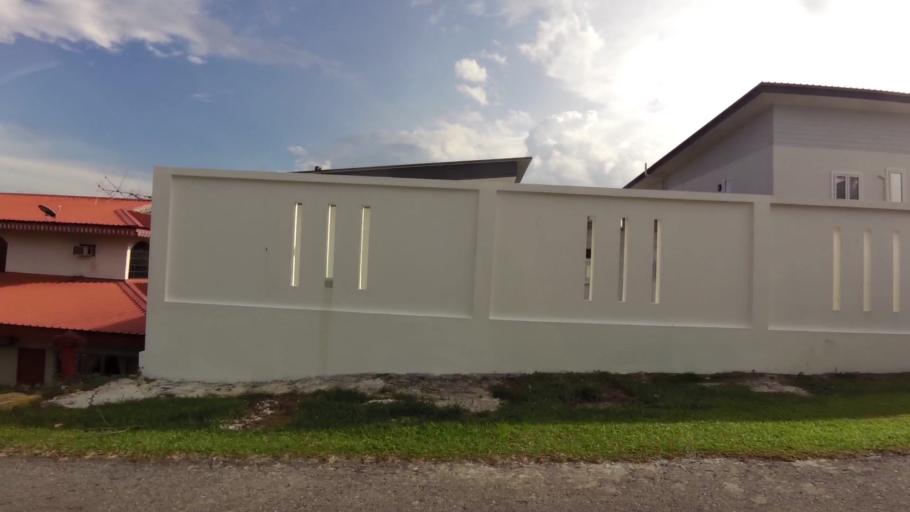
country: BN
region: Brunei and Muara
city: Bandar Seri Begawan
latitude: 4.9674
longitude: 114.9822
